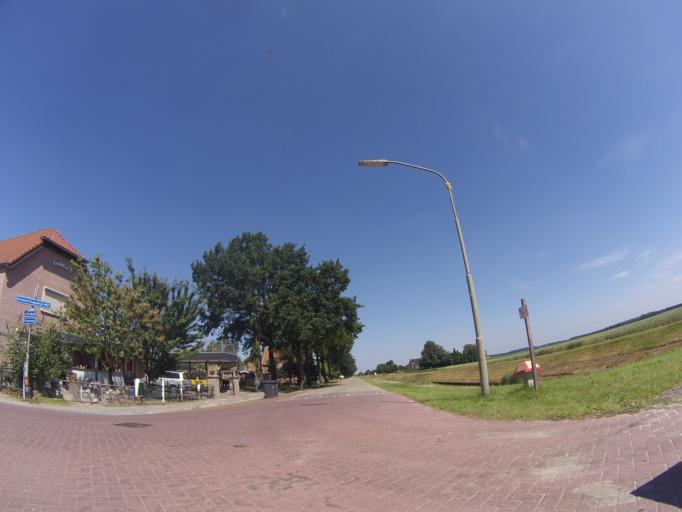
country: NL
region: Drenthe
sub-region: Gemeente Emmen
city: Klazienaveen
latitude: 52.7037
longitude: 7.0452
